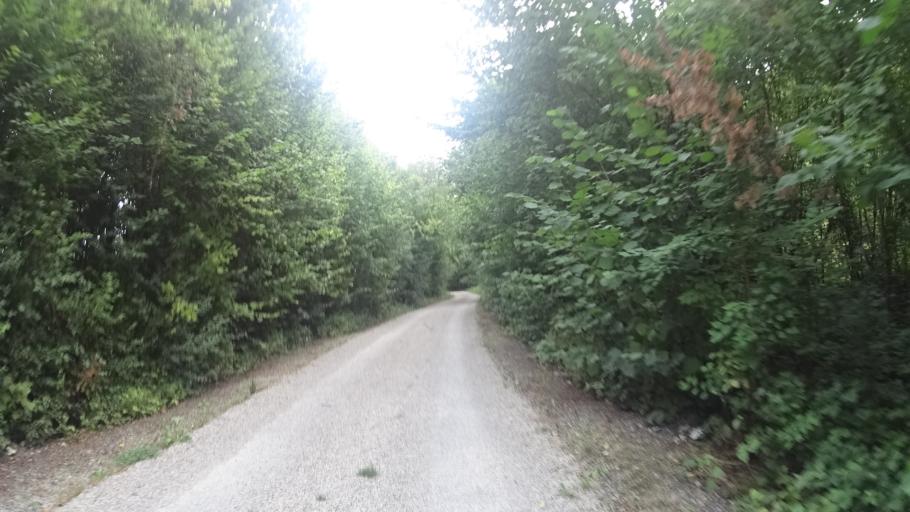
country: FR
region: Picardie
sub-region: Departement de l'Aisne
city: Origny-Sainte-Benoite
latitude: 49.8593
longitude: 3.5092
